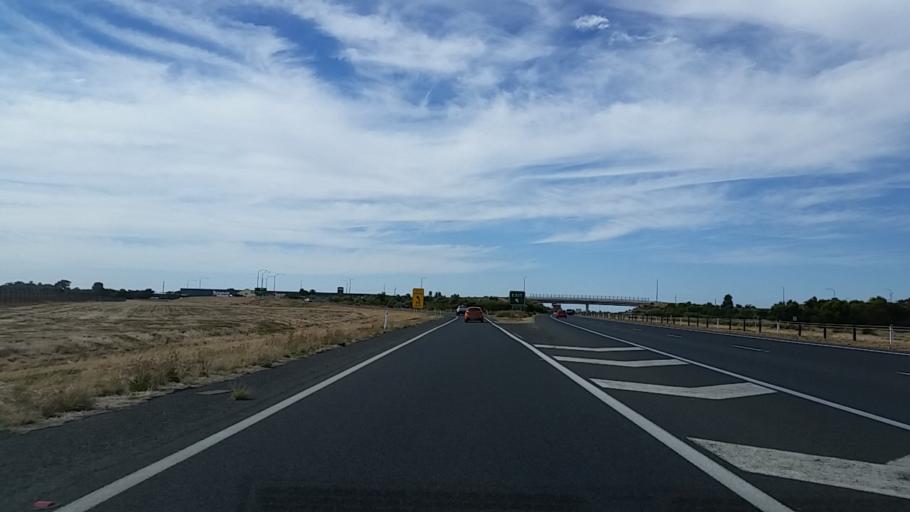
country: AU
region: South Australia
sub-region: Playford
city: Angle Vale
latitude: -34.6662
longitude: 138.6532
